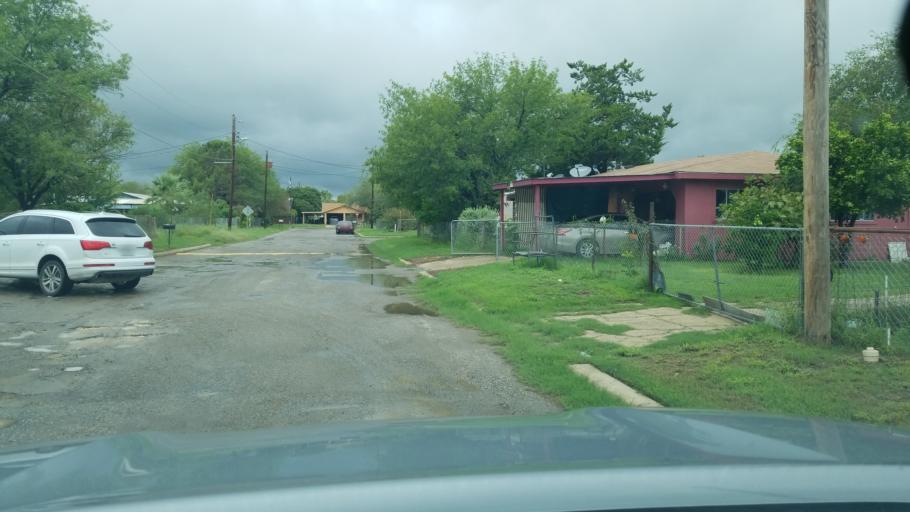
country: US
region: Texas
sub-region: Dimmit County
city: Carrizo Springs
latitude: 28.5315
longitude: -99.8492
